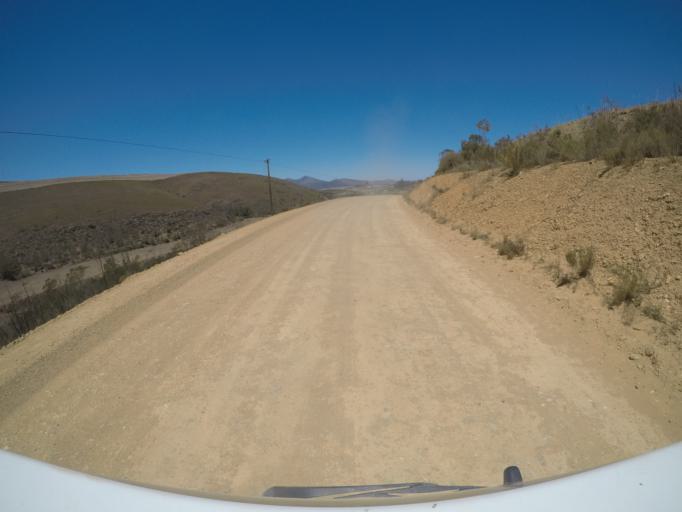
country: ZA
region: Western Cape
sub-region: Overberg District Municipality
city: Grabouw
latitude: -34.2148
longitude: 19.2098
